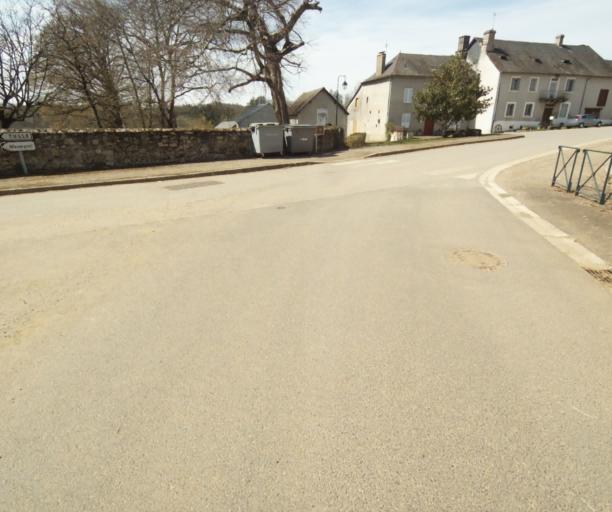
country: FR
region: Limousin
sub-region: Departement de la Correze
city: Seilhac
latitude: 45.3923
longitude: 1.7662
